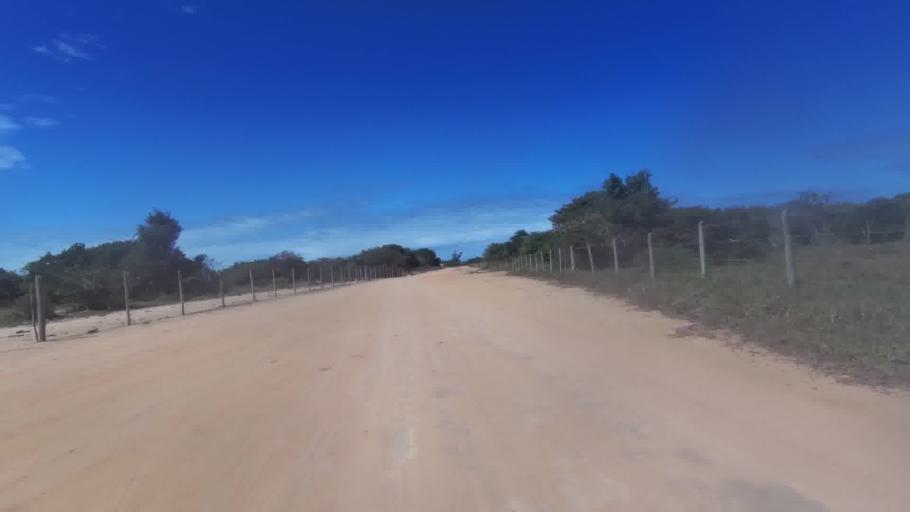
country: BR
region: Espirito Santo
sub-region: Marataizes
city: Marataizes
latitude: -21.1979
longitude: -40.9419
